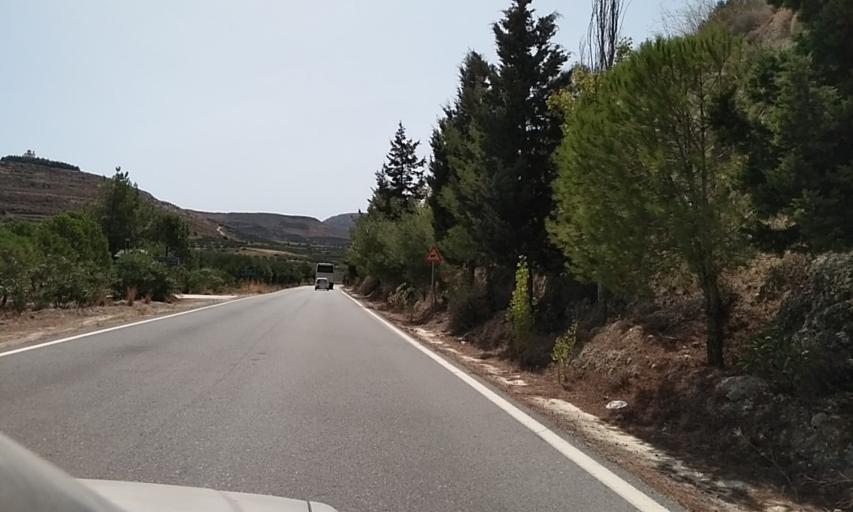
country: GR
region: Crete
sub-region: Nomos Lasithiou
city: Siteia
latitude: 35.1074
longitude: 26.0593
